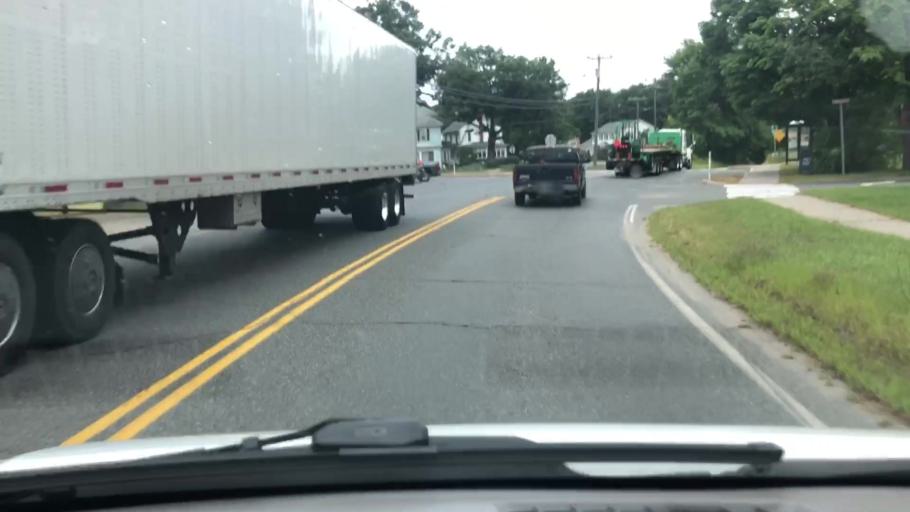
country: US
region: Massachusetts
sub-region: Franklin County
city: Turners Falls
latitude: 42.5996
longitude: -72.5514
